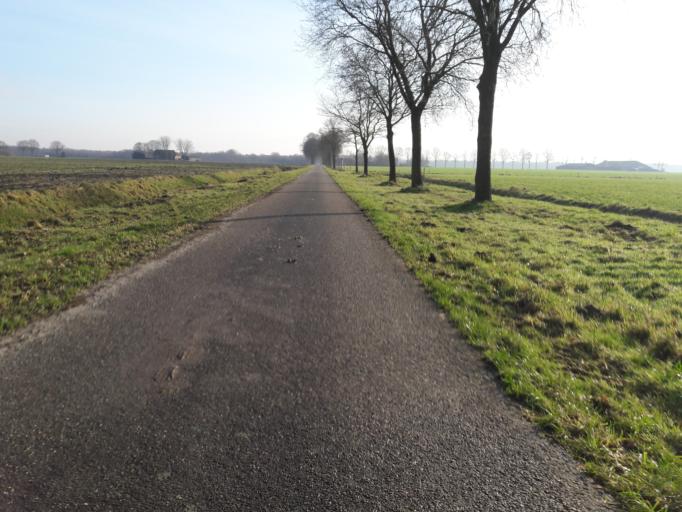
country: NL
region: Drenthe
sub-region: Gemeente Assen
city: Assen
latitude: 52.9471
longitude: 6.6442
